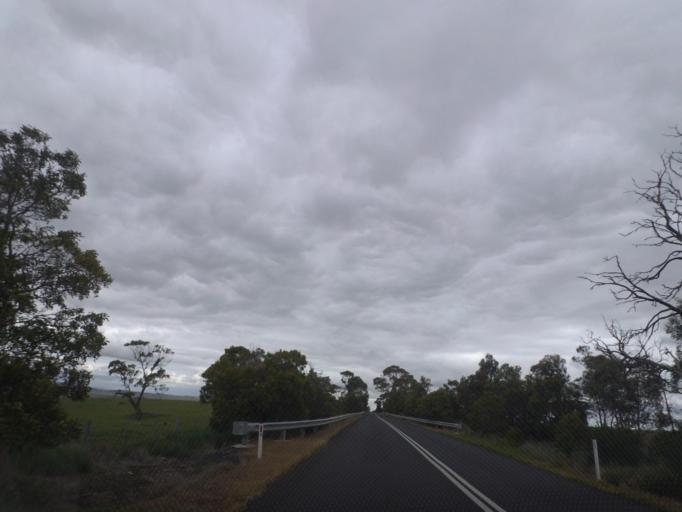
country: AU
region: Victoria
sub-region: Hume
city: Sunbury
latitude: -37.3871
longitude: 144.8307
